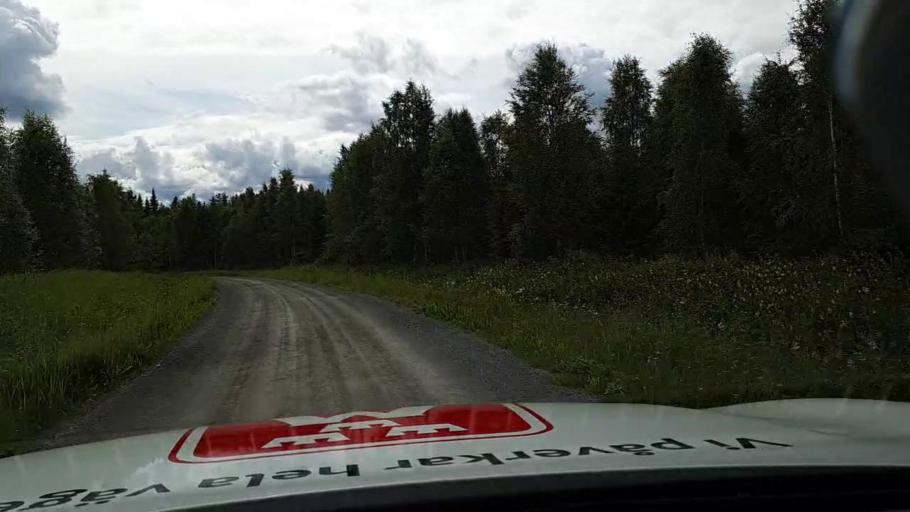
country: SE
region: Jaemtland
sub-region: OEstersunds Kommun
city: Lit
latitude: 63.3015
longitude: 15.2454
